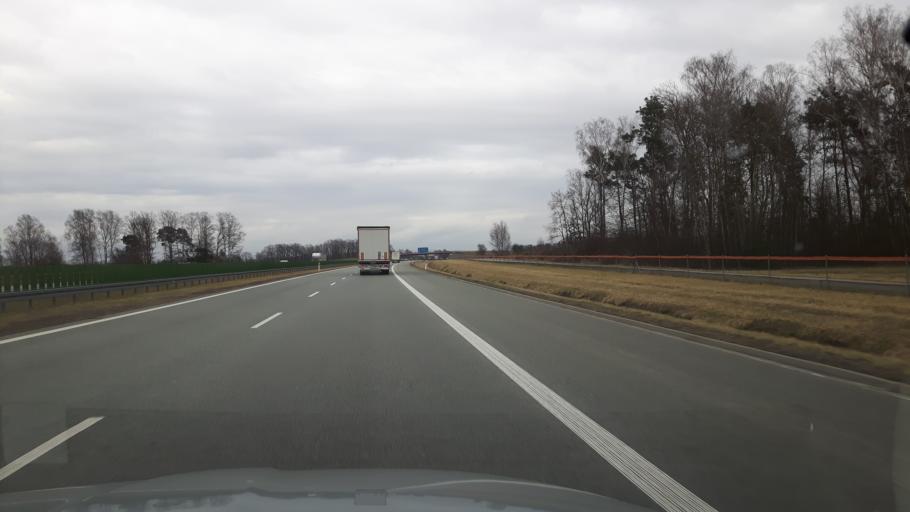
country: PL
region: Masovian Voivodeship
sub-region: Powiat minski
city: Jakubow
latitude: 52.2160
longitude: 21.6250
